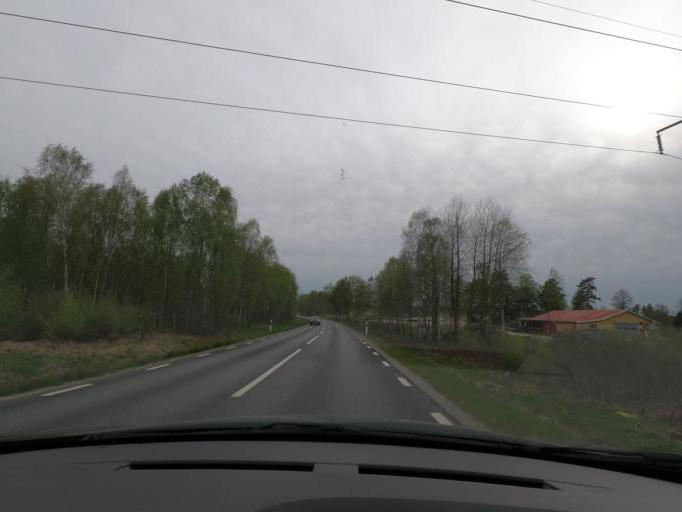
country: SE
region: Joenkoeping
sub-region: Varnamo Kommun
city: Bredaryd
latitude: 57.2138
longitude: 13.7707
